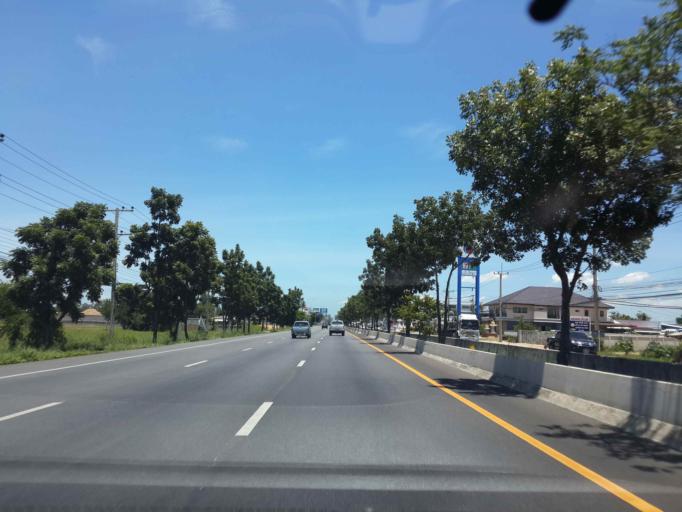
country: TH
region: Phetchaburi
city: Tha Yang
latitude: 12.9581
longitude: 99.9011
